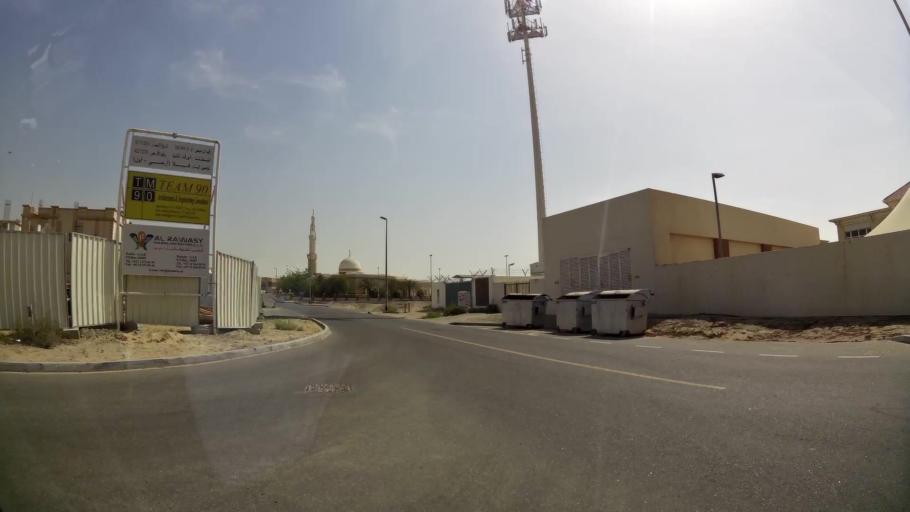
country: AE
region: Ash Shariqah
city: Sharjah
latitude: 25.2009
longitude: 55.4085
